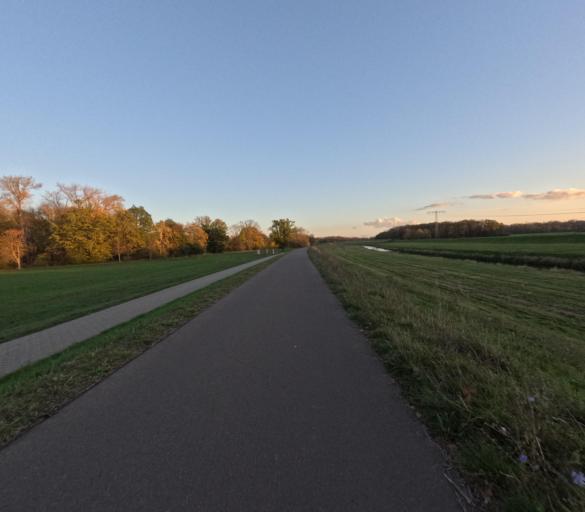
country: DE
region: Saxony
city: Schkeuditz
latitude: 51.3786
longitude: 12.2754
